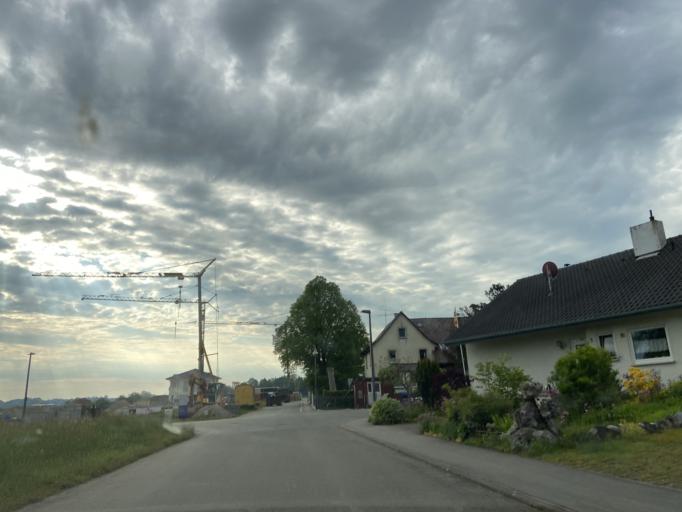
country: DE
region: Baden-Wuerttemberg
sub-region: Tuebingen Region
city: Hohentengen
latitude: 48.0366
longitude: 9.3720
